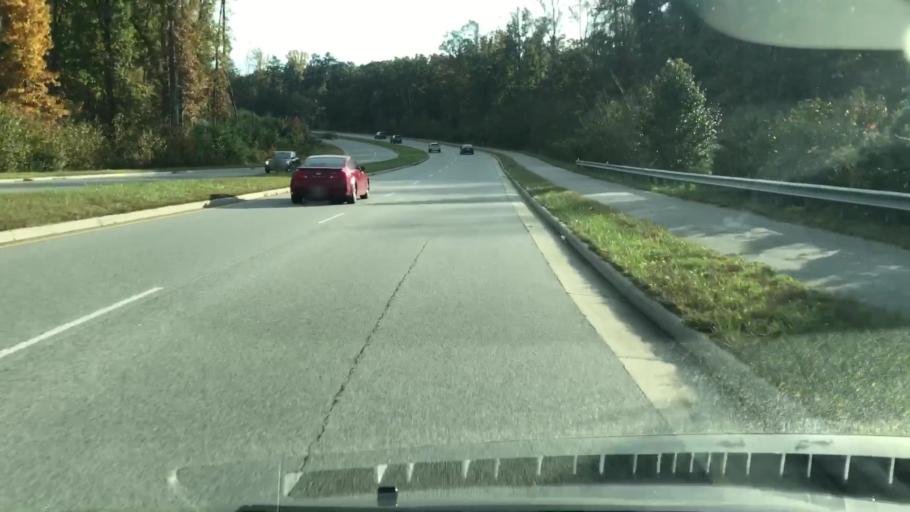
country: US
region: Virginia
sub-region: Fairfax County
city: Hayfield
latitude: 38.7396
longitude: -77.1474
